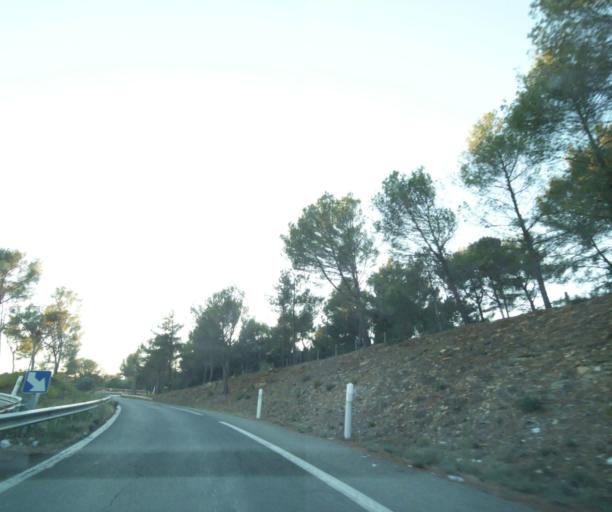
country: FR
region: Provence-Alpes-Cote d'Azur
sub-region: Departement du Var
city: Saint-Cyr-sur-Mer
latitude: 43.1948
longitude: 5.6882
